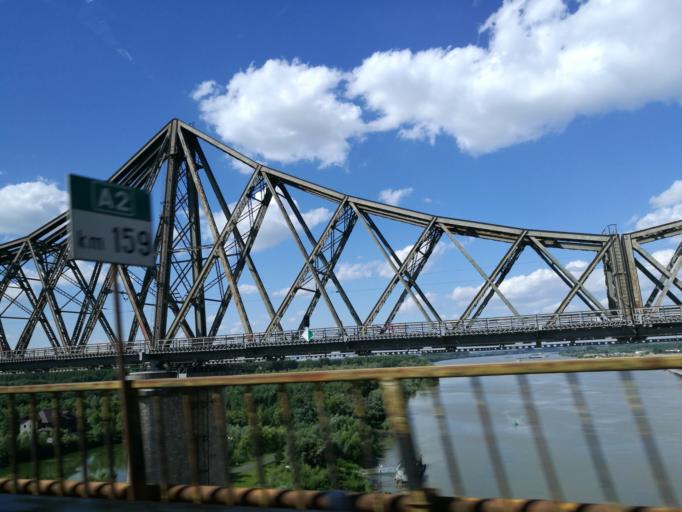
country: RO
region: Constanta
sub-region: Oras Cernavoda
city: Cernavoda
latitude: 44.3413
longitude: 28.0183
